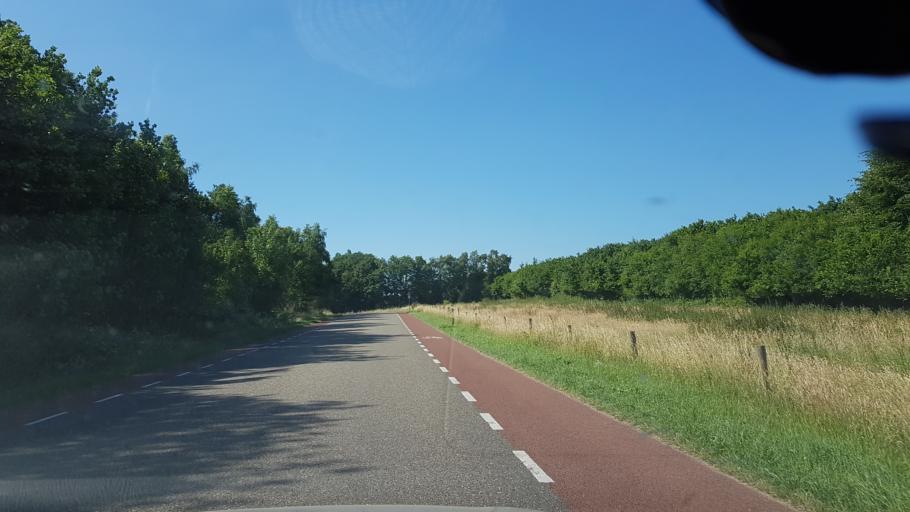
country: NL
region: Gelderland
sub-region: Gemeente Groesbeek
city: Bredeweg
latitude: 51.7437
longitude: 5.9525
